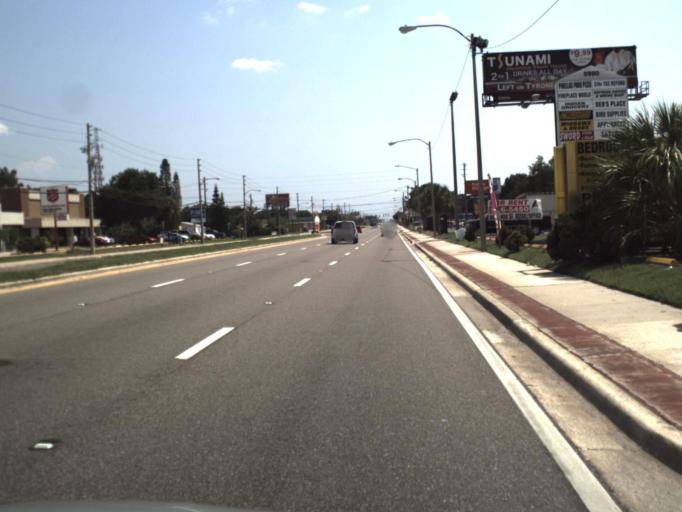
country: US
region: Florida
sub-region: Pinellas County
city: Kenneth City
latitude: 27.8264
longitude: -82.7286
